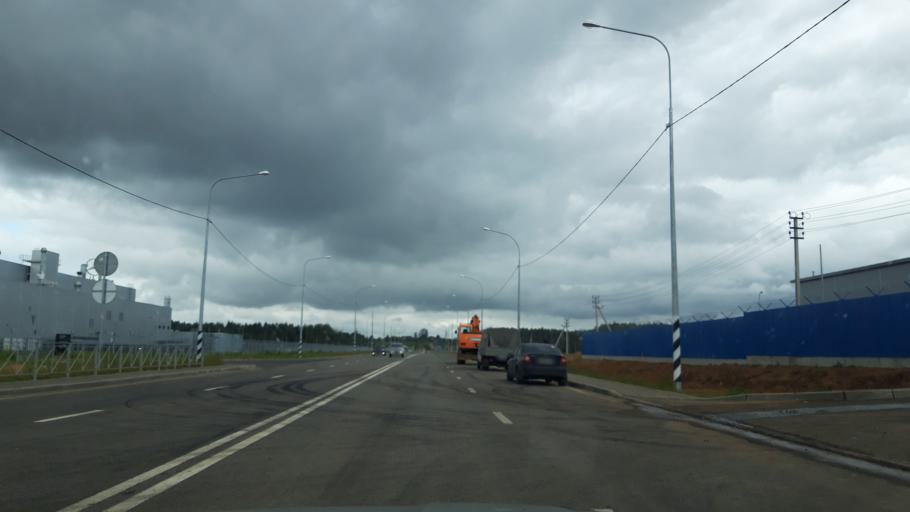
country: RU
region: Moskovskaya
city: Lozhki
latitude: 56.0830
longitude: 37.0871
